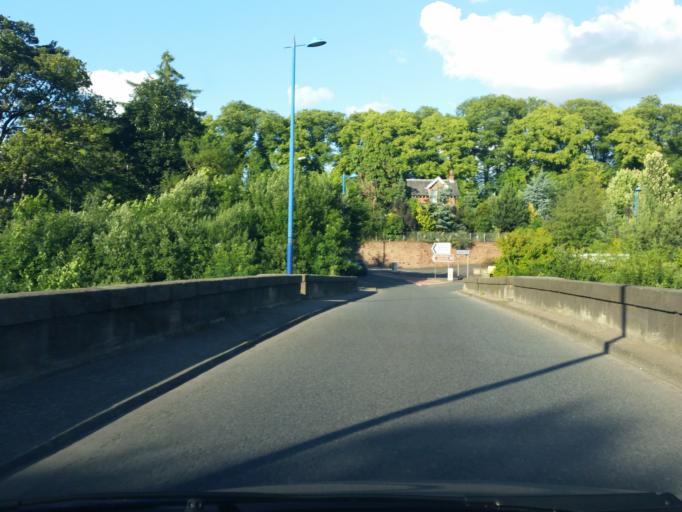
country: GB
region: Scotland
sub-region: South Lanarkshire
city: Dalserf
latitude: 55.7376
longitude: -3.9231
